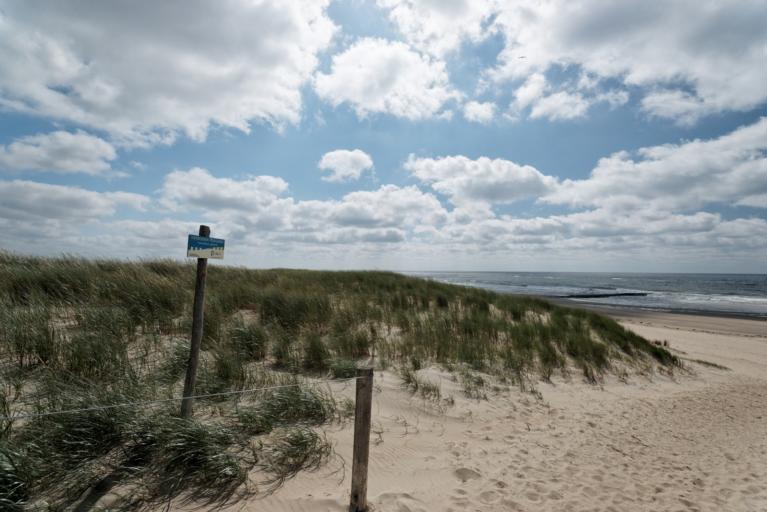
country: NL
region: North Holland
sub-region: Gemeente Texel
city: Den Burg
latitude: 53.0754
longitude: 4.7322
